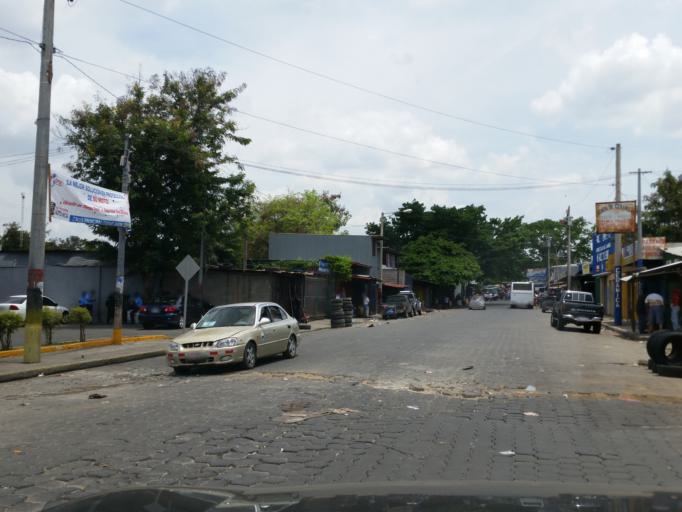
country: NI
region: Managua
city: Managua
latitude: 12.1534
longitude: -86.2586
